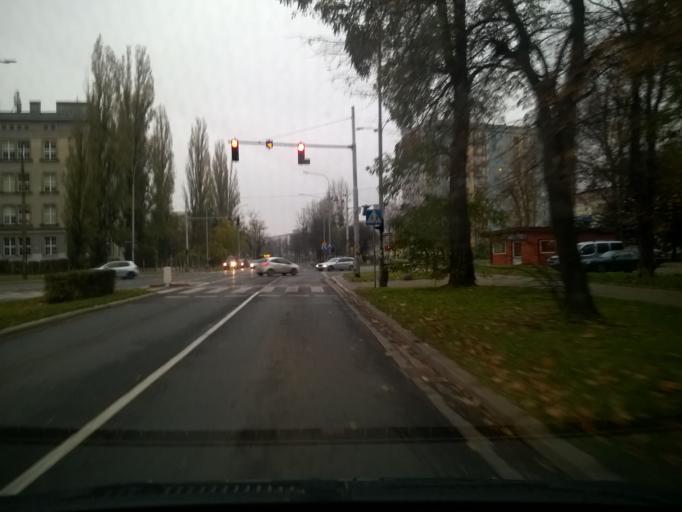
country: PL
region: Lower Silesian Voivodeship
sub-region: Powiat wroclawski
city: Wroclaw
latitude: 51.0884
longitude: 17.0340
